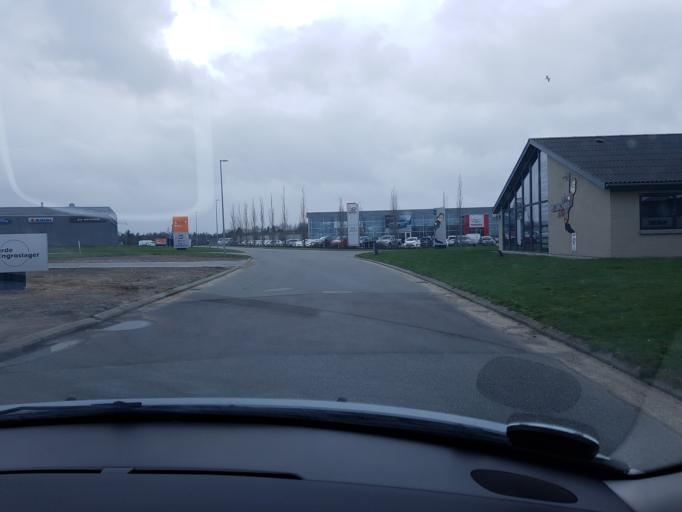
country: DK
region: South Denmark
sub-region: Varde Kommune
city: Varde
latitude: 55.6010
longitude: 8.4996
